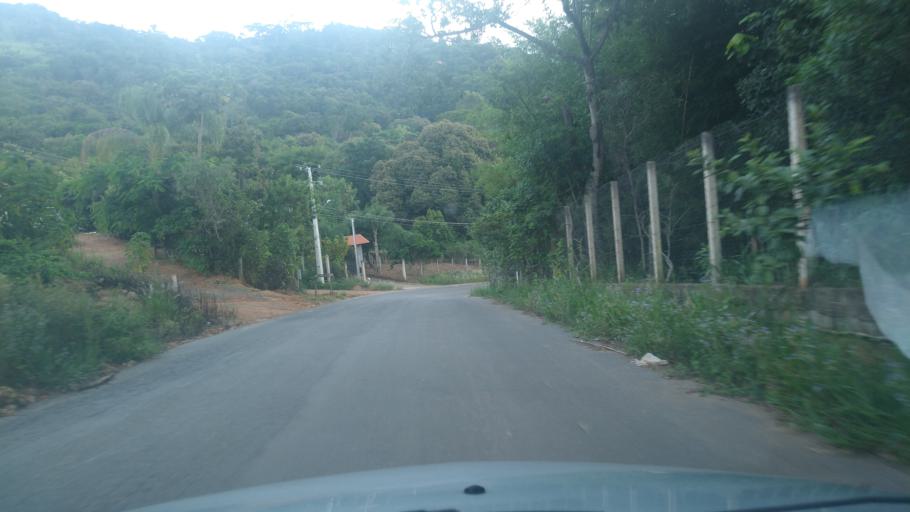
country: BR
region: Minas Gerais
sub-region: Extrema
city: Extrema
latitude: -22.7191
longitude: -46.3391
